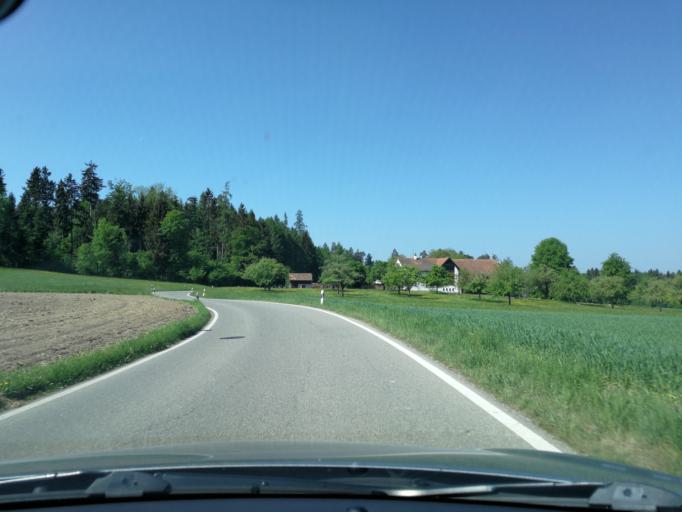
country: CH
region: Zurich
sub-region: Bezirk Meilen
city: Zumikon
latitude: 47.3160
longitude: 8.6196
